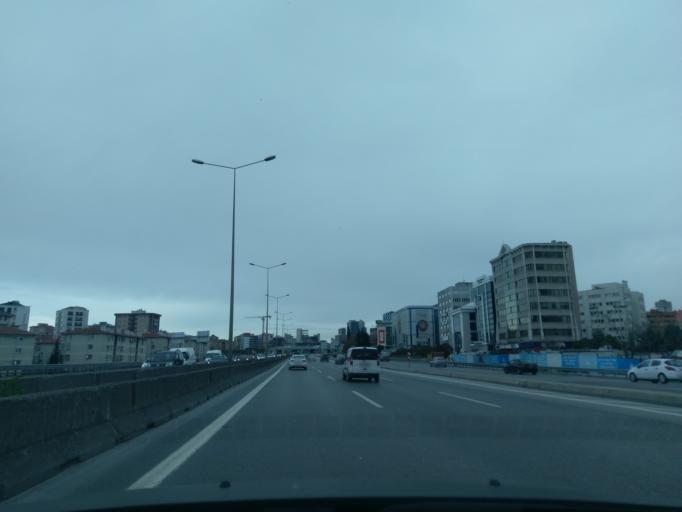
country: TR
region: Istanbul
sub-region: Atasehir
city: Atasehir
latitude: 40.9609
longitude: 29.1094
